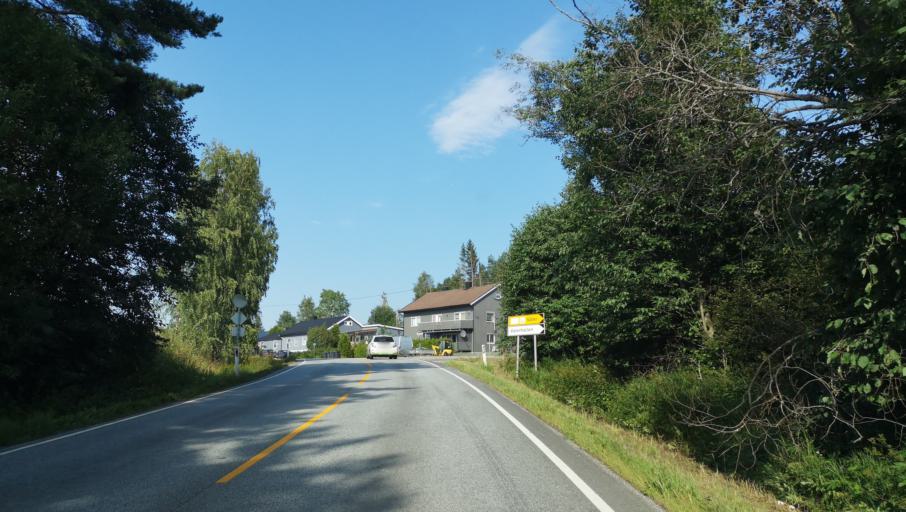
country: NO
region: Ostfold
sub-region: Valer
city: Kirkebygda
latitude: 59.4966
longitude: 10.8390
